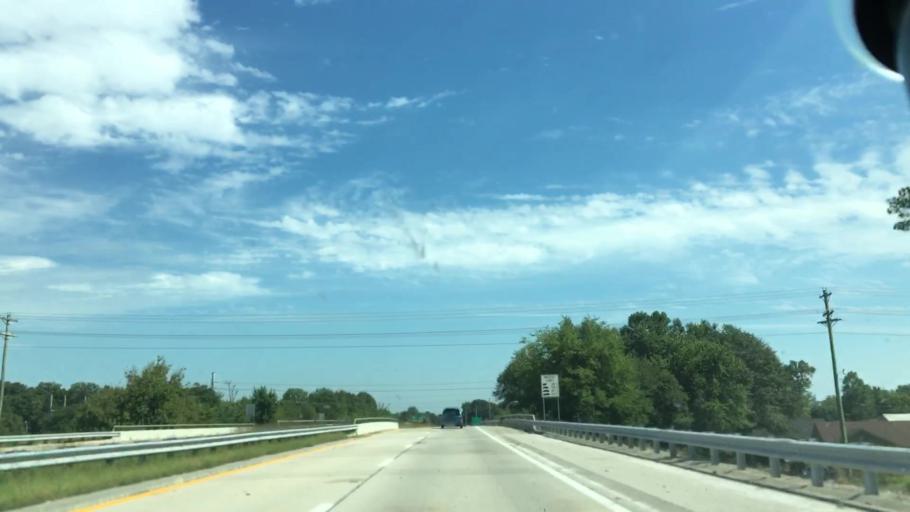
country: US
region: Kentucky
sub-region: Daviess County
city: Owensboro
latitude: 37.7662
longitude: -87.1778
